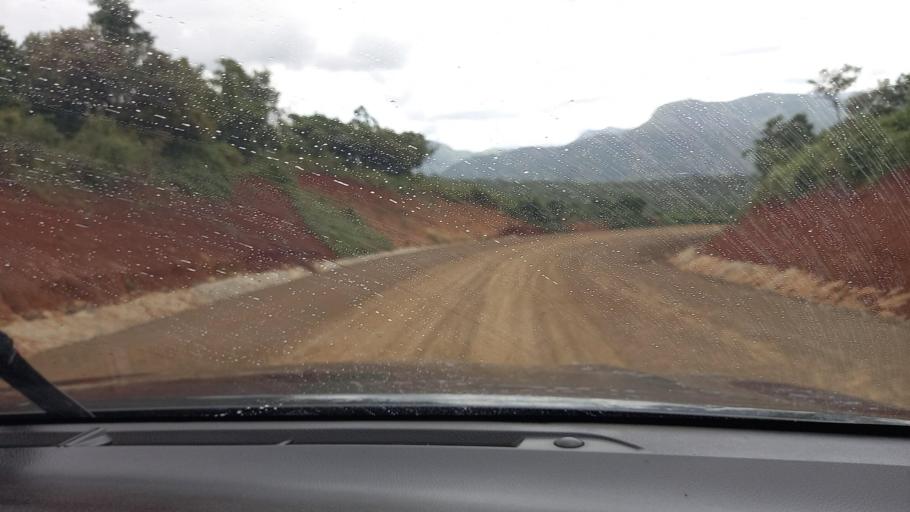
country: ET
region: Southern Nations, Nationalities, and People's Region
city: Mizan Teferi
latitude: 6.1813
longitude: 35.6975
